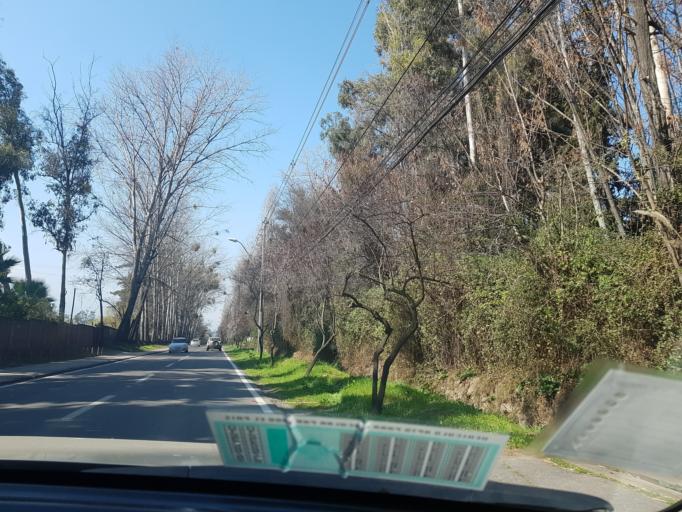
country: CL
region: Santiago Metropolitan
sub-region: Provincia de Cordillera
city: Puente Alto
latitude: -33.6327
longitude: -70.5655
